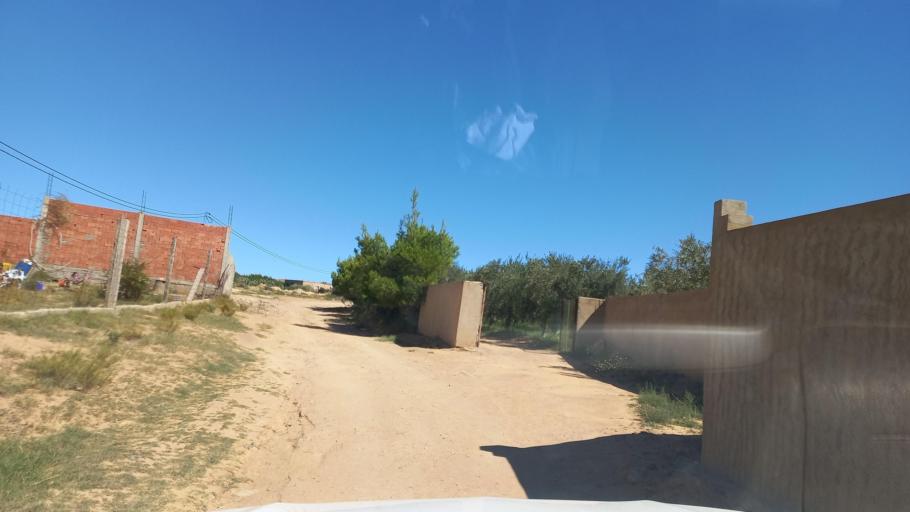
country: TN
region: Al Qasrayn
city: Sbiba
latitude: 35.3459
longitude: 9.0936
